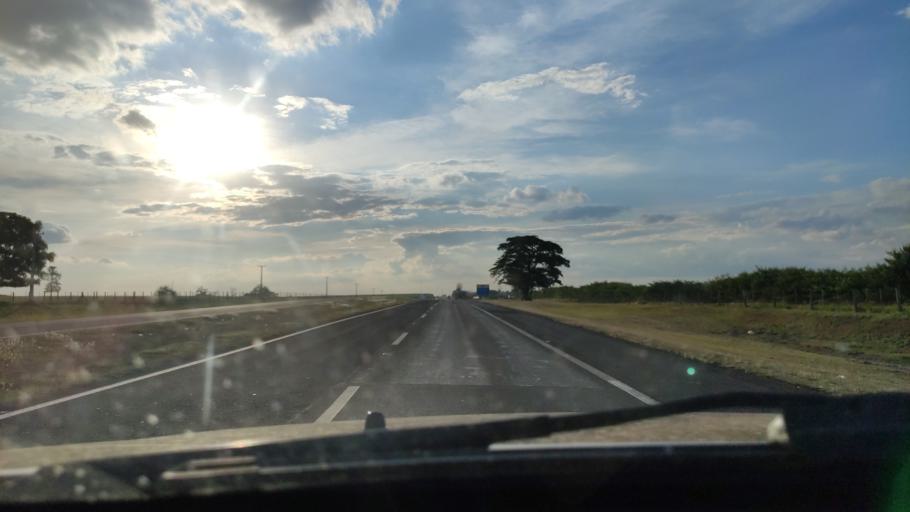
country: BR
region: Sao Paulo
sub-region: Rancharia
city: Rancharia
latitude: -22.4550
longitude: -50.9743
